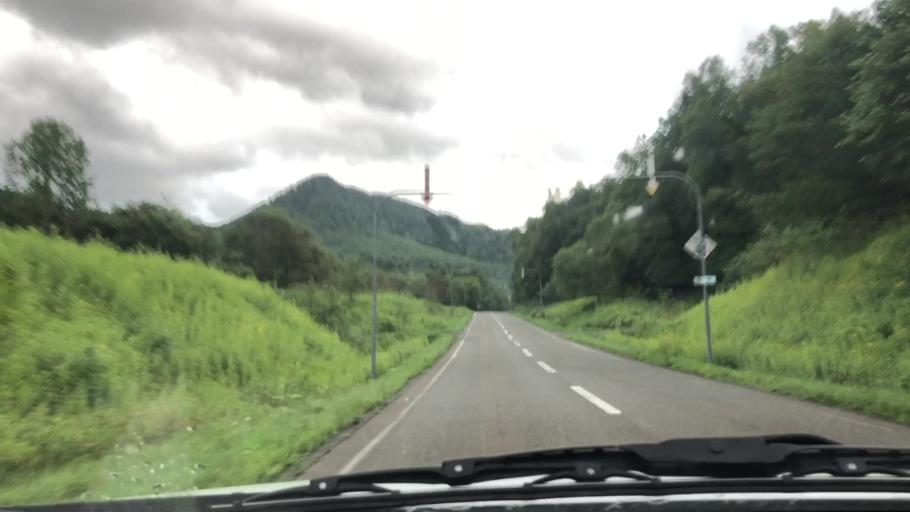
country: JP
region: Hokkaido
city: Shimo-furano
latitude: 42.9256
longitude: 142.3745
